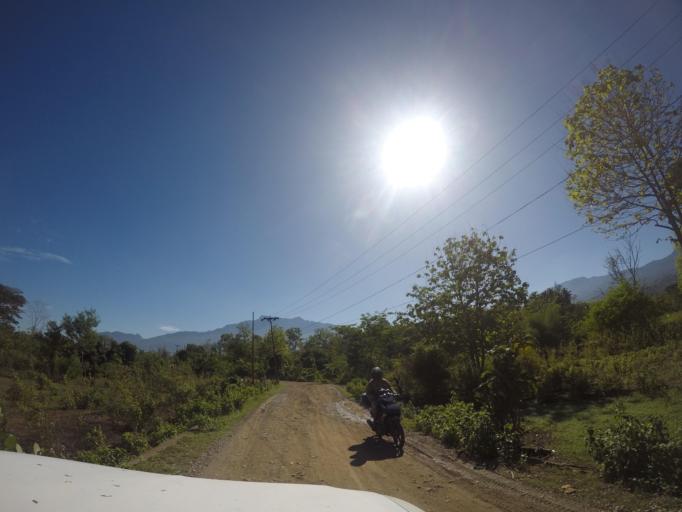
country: TL
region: Bobonaro
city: Maliana
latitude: -8.9978
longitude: 125.1976
